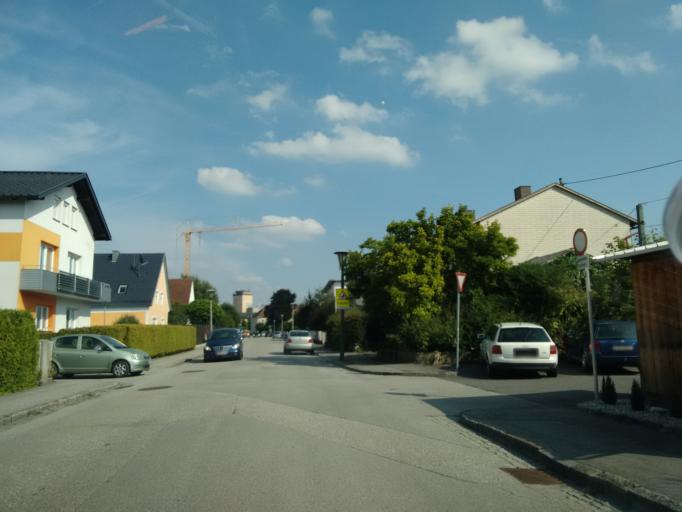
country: AT
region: Upper Austria
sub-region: Politischer Bezirk Grieskirchen
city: Grieskirchen
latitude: 48.2350
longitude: 13.8223
